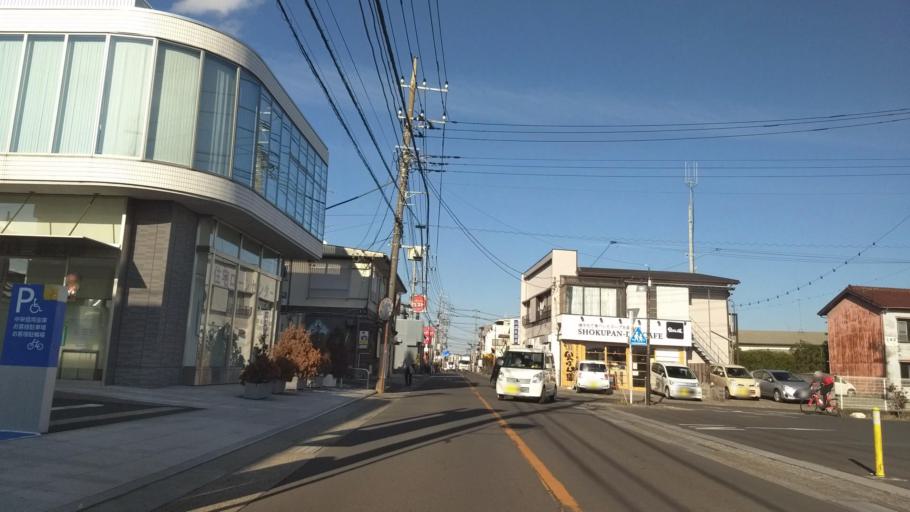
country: JP
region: Kanagawa
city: Isehara
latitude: 35.3756
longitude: 139.2764
